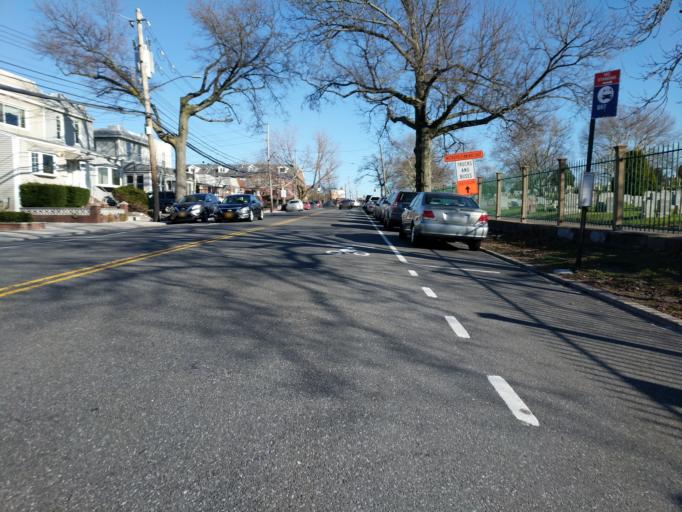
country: US
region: New York
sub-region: Kings County
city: East New York
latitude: 40.7169
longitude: -73.8889
